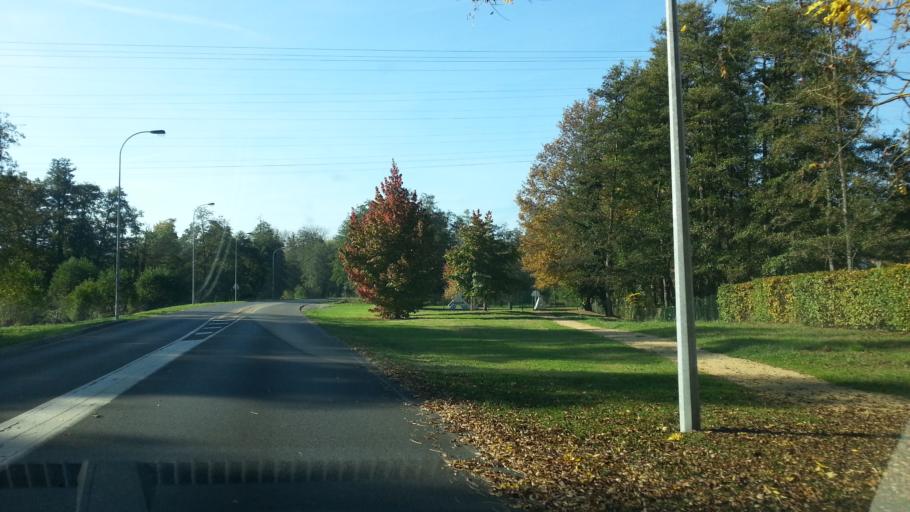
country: FR
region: Picardie
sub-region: Departement de l'Oise
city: Thiverny
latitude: 49.2554
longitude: 2.4203
